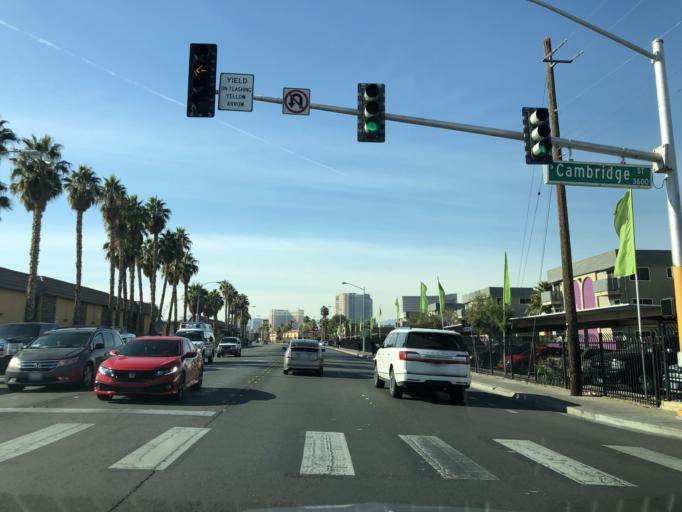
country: US
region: Nevada
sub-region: Clark County
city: Winchester
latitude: 36.1222
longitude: -115.1418
